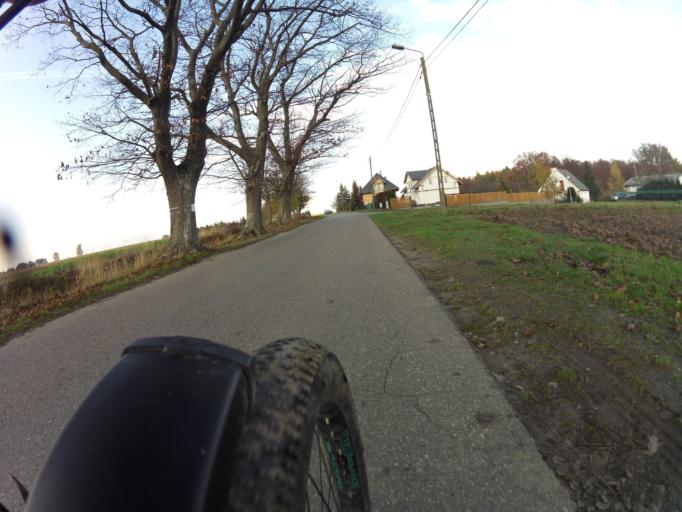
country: PL
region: Pomeranian Voivodeship
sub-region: Powiat pucki
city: Krokowa
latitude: 54.7544
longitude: 18.1847
